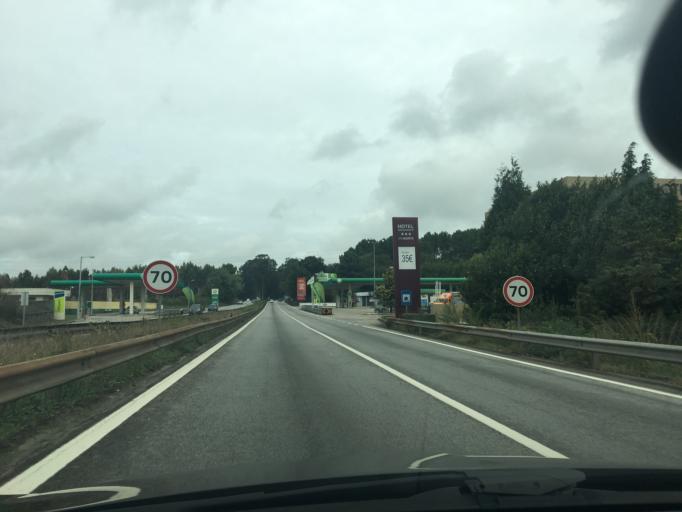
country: PT
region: Porto
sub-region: Maia
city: Leca do Bailio
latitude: 41.2175
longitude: -8.6269
